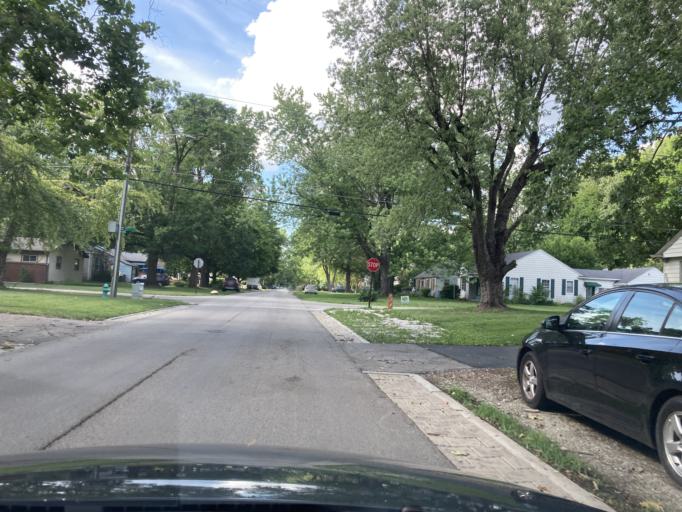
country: US
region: Indiana
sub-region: Marion County
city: Broad Ripple
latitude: 39.8566
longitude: -86.1339
